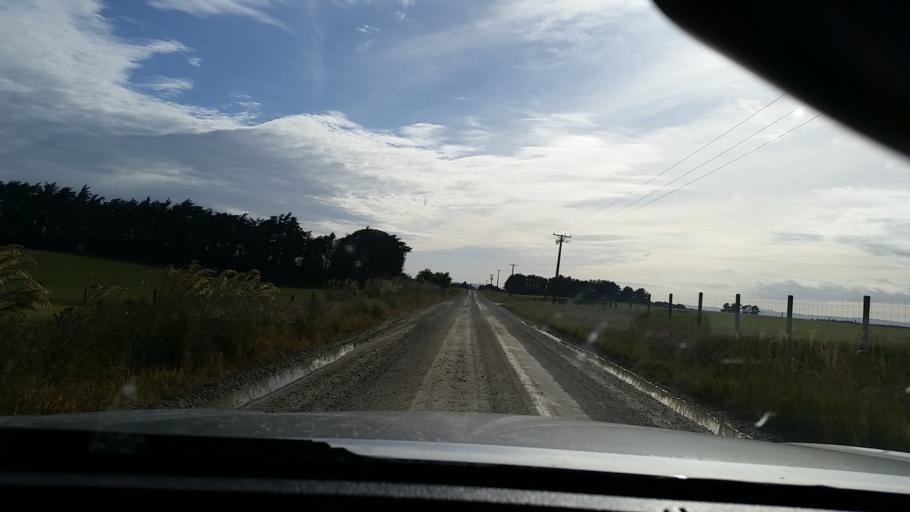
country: NZ
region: Southland
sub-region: Gore District
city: Gore
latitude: -46.2777
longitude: 168.6992
